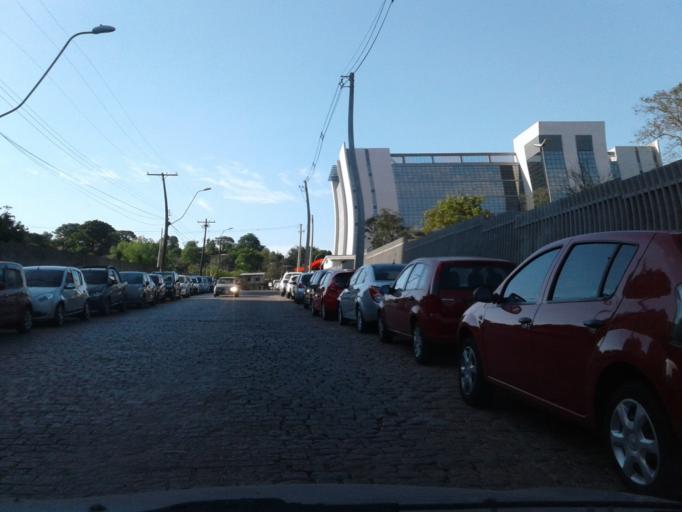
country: BR
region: Rio Grande do Sul
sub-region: Porto Alegre
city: Porto Alegre
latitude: -30.0532
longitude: -51.1595
